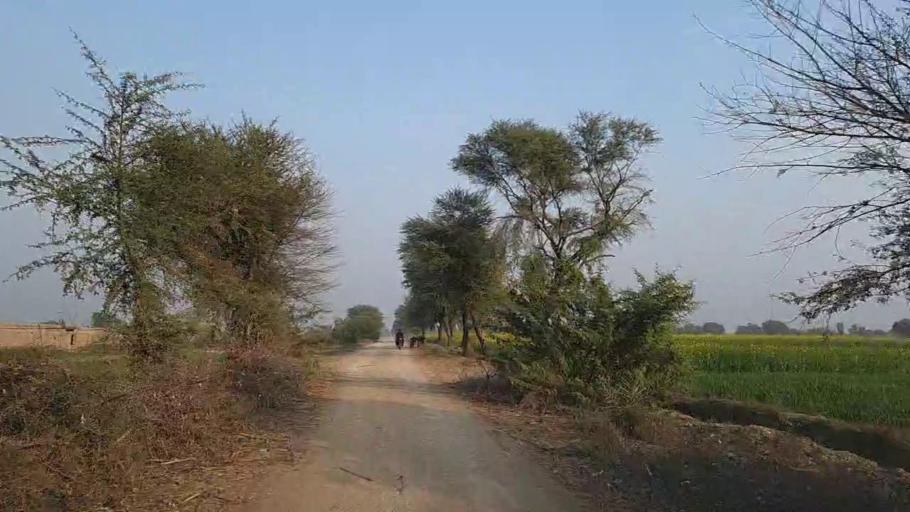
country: PK
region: Sindh
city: Jam Sahib
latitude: 26.3207
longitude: 68.5822
